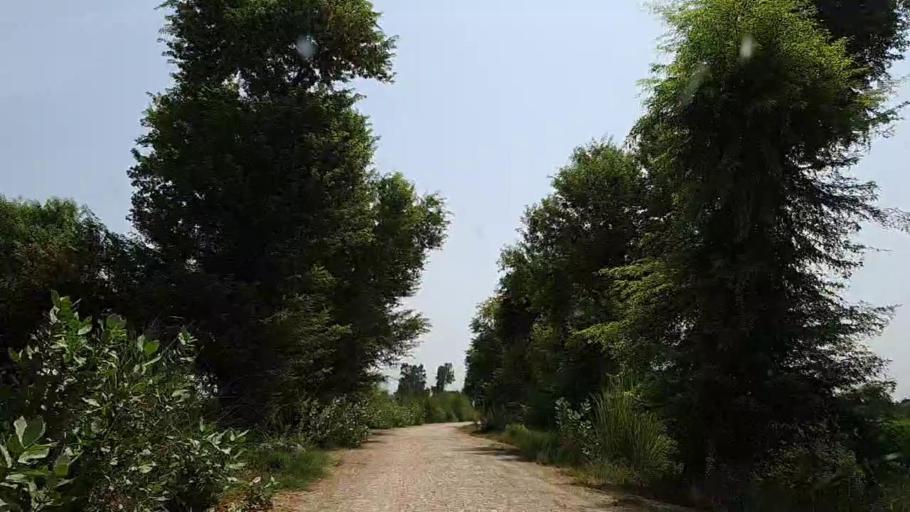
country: PK
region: Sindh
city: Adilpur
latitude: 27.9341
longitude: 69.3923
